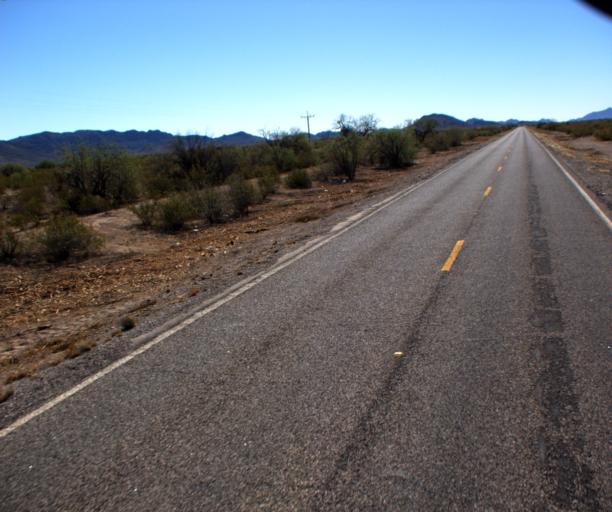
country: US
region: Arizona
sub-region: Pima County
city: Ajo
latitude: 32.3207
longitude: -112.7702
